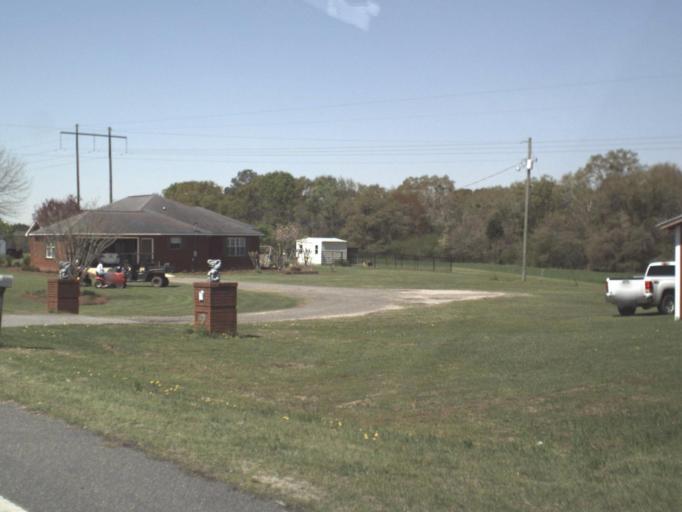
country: US
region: Florida
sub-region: Jackson County
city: Graceville
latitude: 30.9638
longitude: -85.5821
